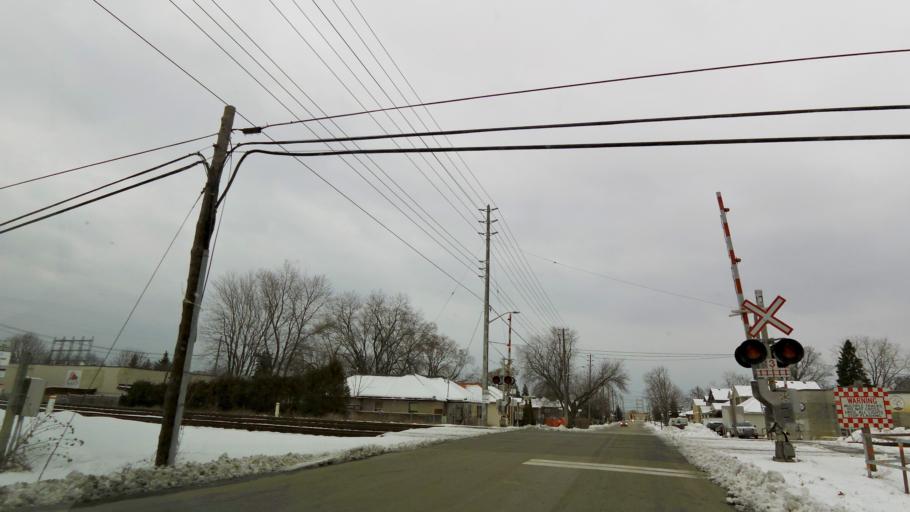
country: CA
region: Ontario
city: Etobicoke
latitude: 43.5793
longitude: -79.5621
